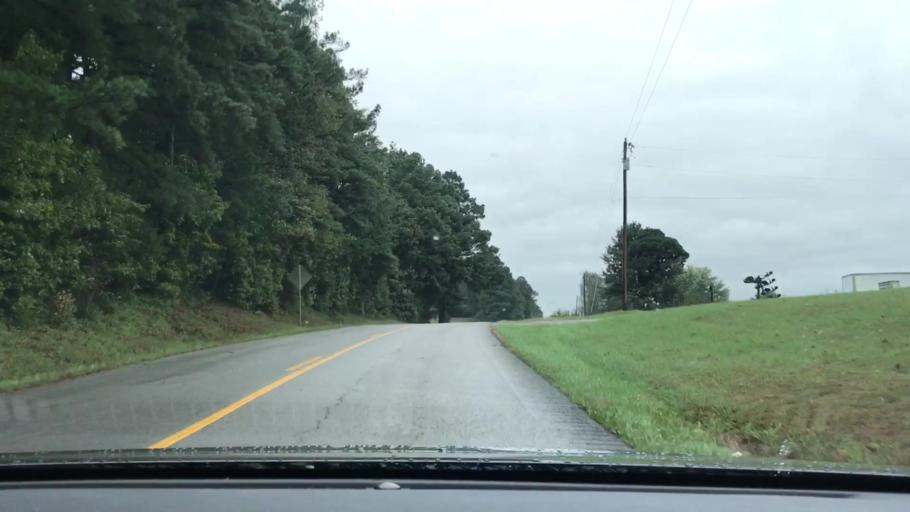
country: US
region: Kentucky
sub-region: McLean County
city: Calhoun
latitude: 37.4806
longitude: -87.2461
